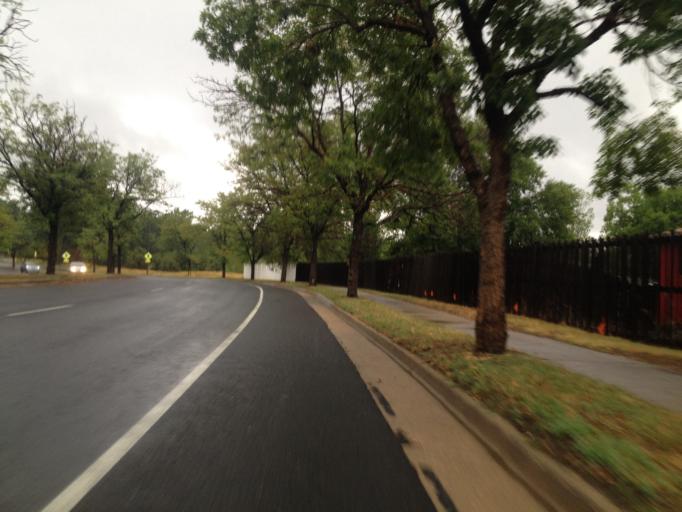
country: US
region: Colorado
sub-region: Boulder County
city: Louisville
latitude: 39.9817
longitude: -105.1445
